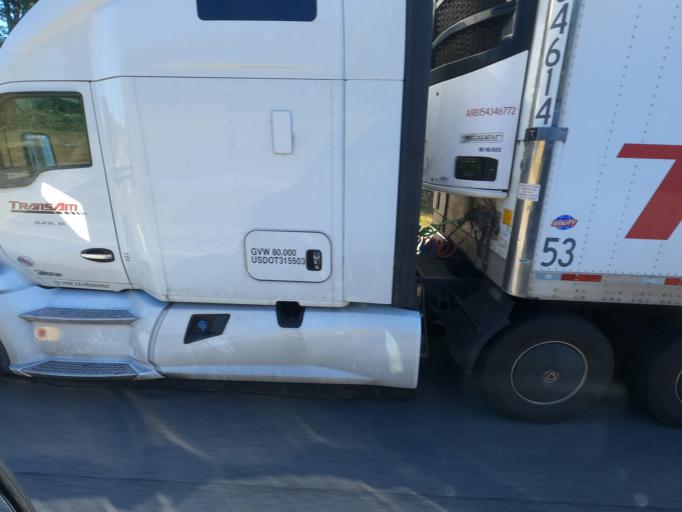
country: US
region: Tennessee
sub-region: Williamson County
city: Thompson's Station
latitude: 35.8368
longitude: -87.0612
